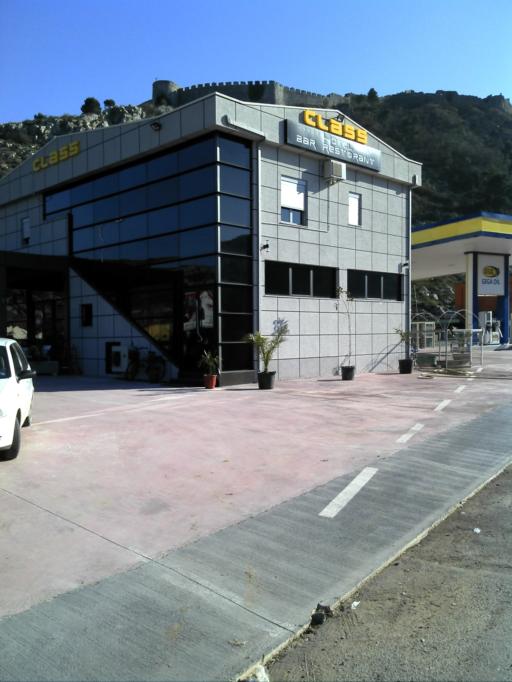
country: AL
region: Shkoder
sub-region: Rrethi i Shkodres
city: Shkoder
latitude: 42.0493
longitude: 19.4923
